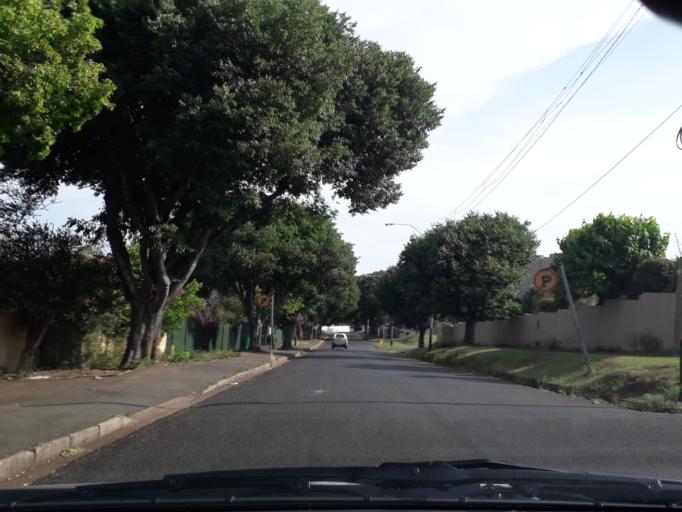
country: ZA
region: Gauteng
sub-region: City of Johannesburg Metropolitan Municipality
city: Johannesburg
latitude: -26.1747
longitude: 28.0976
